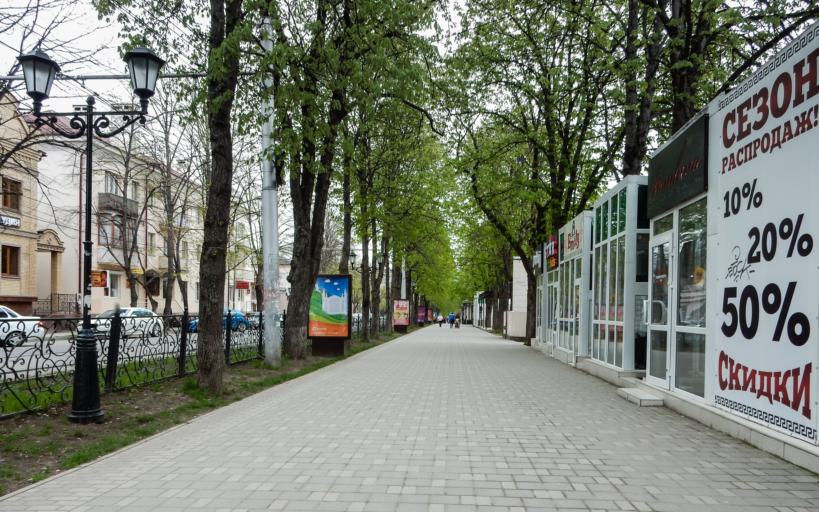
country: RU
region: Stavropol'skiy
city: Pyatigorsk
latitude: 44.0359
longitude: 43.0669
